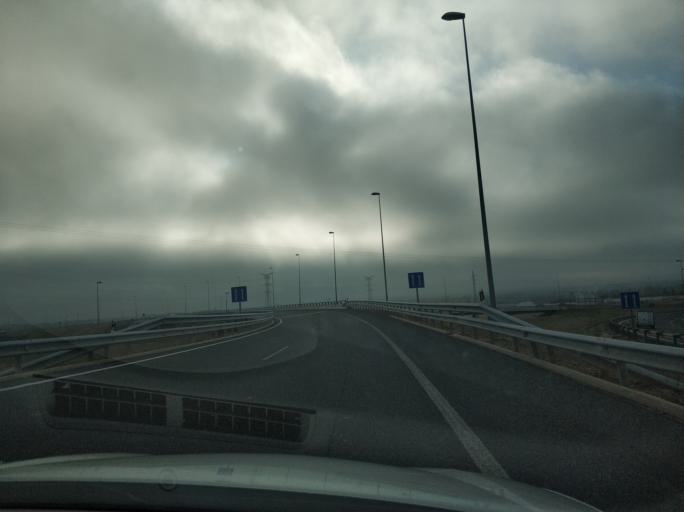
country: ES
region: Castille and Leon
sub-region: Provincia de Leon
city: Leon
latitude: 42.5717
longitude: -5.5431
